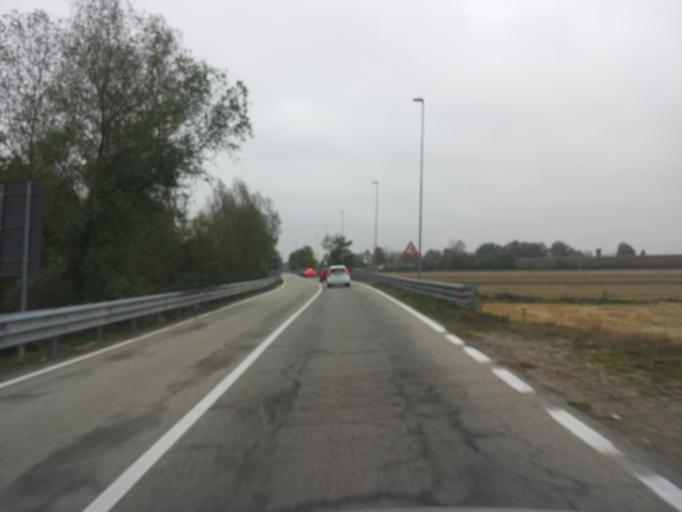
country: IT
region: Piedmont
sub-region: Provincia di Vercelli
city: Borgo Vercelli
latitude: 45.3630
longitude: 8.4779
